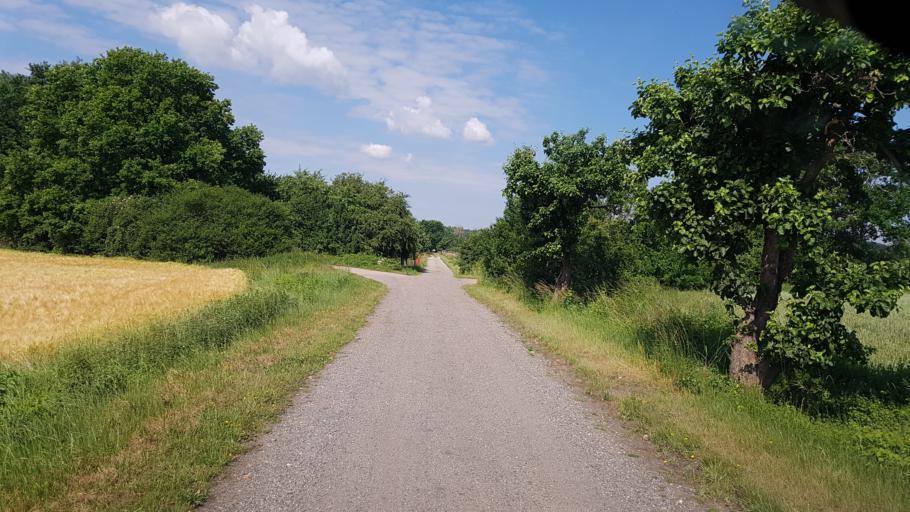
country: DE
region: Brandenburg
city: Doberlug-Kirchhain
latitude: 51.6240
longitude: 13.5424
